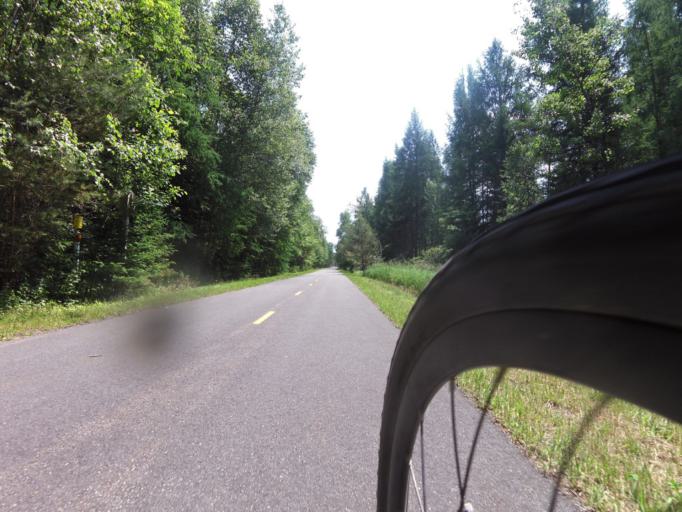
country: CA
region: Quebec
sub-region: Laurentides
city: Mont-Tremblant
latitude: 46.1332
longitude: -74.5944
